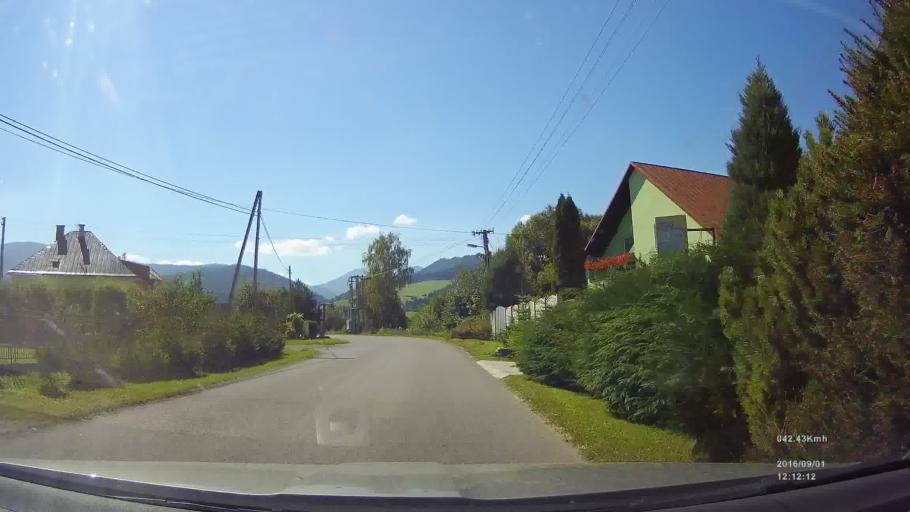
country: SK
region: Zilinsky
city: Ruzomberok
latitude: 49.0591
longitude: 19.4316
